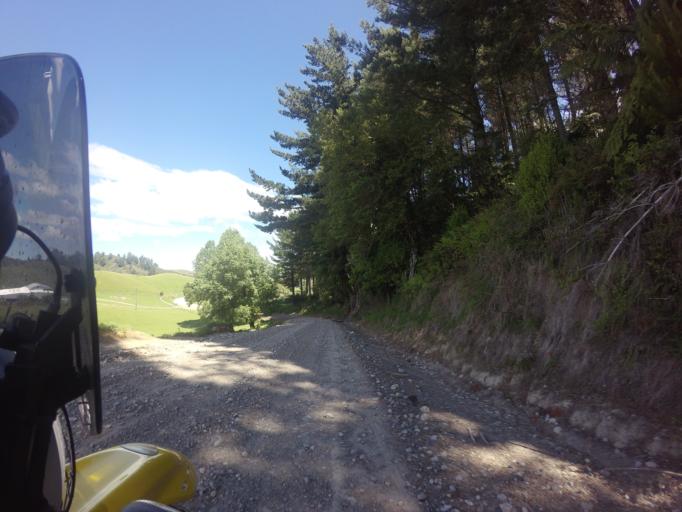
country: NZ
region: Hawke's Bay
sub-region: Wairoa District
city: Wairoa
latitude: -38.9723
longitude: 177.7032
